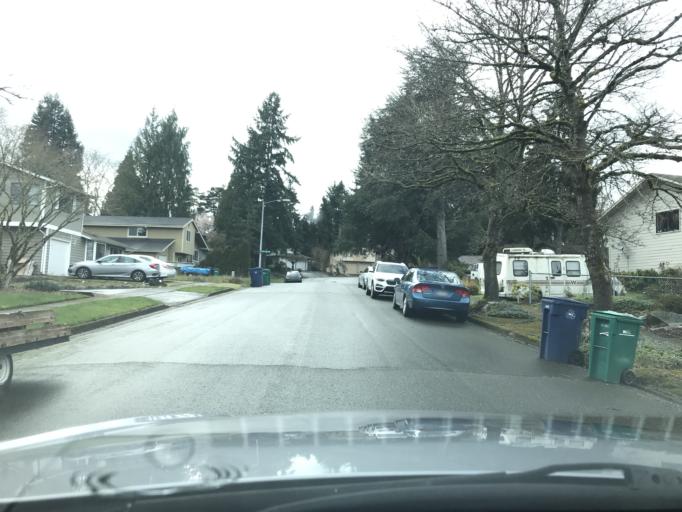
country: US
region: Washington
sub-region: King County
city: Redmond
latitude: 47.6556
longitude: -122.1302
